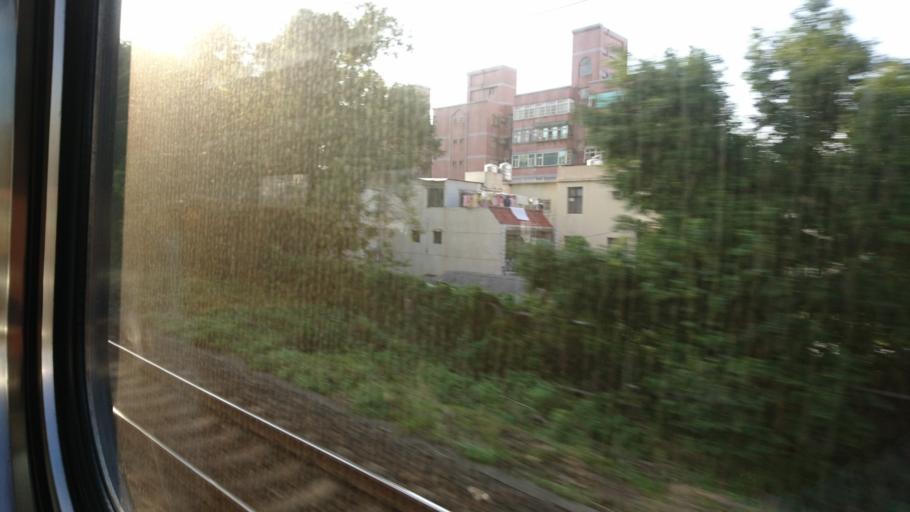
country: TW
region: Taiwan
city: Daxi
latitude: 24.9428
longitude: 121.2145
